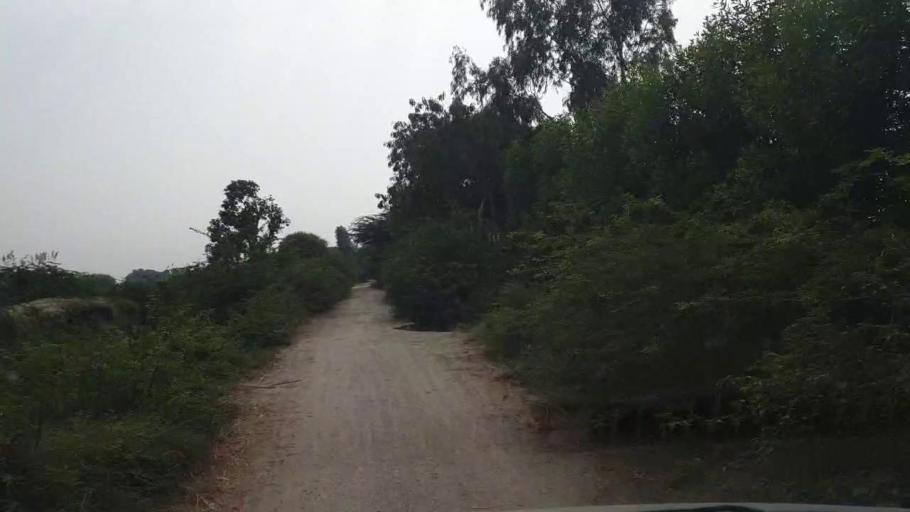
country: PK
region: Sindh
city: Matli
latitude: 25.0001
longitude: 68.7018
